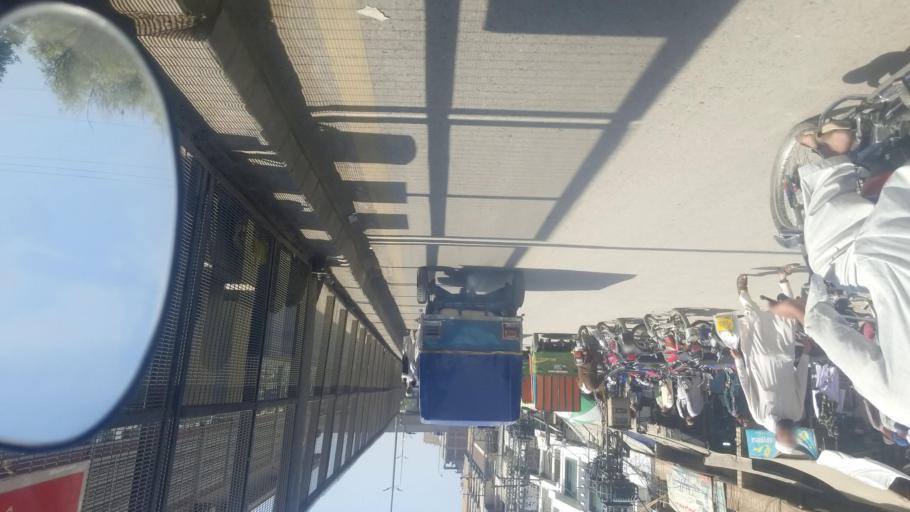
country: PK
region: Khyber Pakhtunkhwa
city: Peshawar
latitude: 34.0157
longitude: 71.5723
